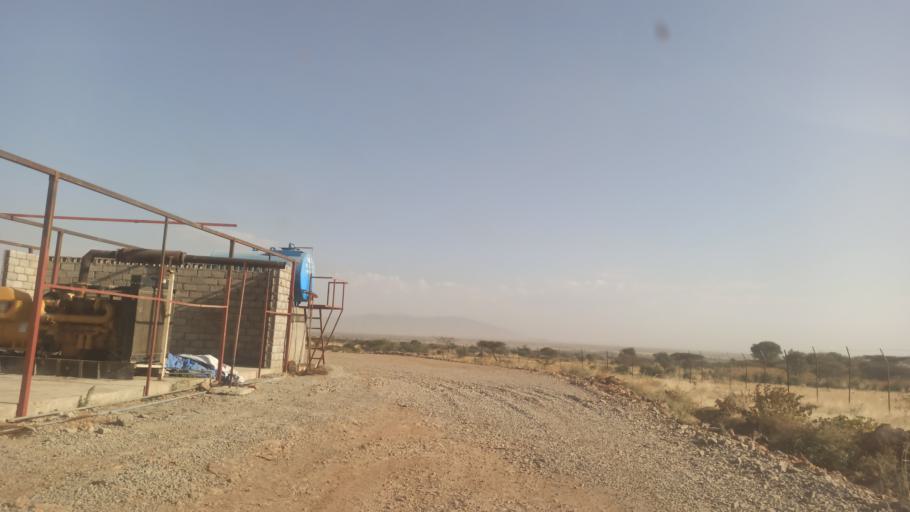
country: ET
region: Oromiya
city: Ziway
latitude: 7.9313
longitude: 38.6167
